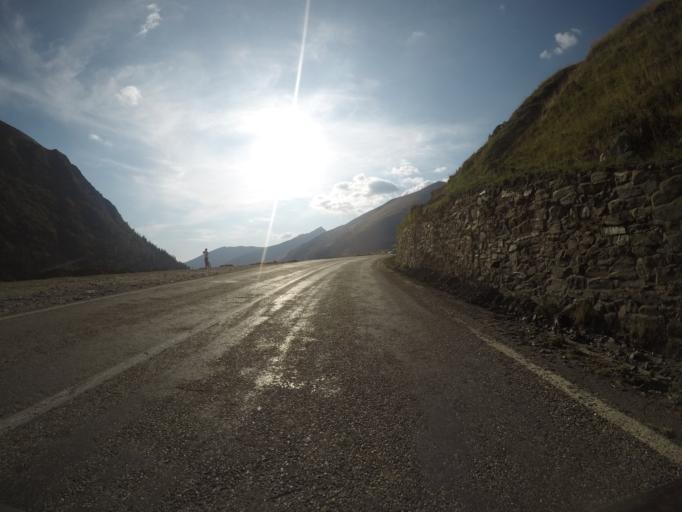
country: RO
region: Sibiu
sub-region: Comuna Cartisoara
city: Cartisoara
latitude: 45.5852
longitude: 24.6375
